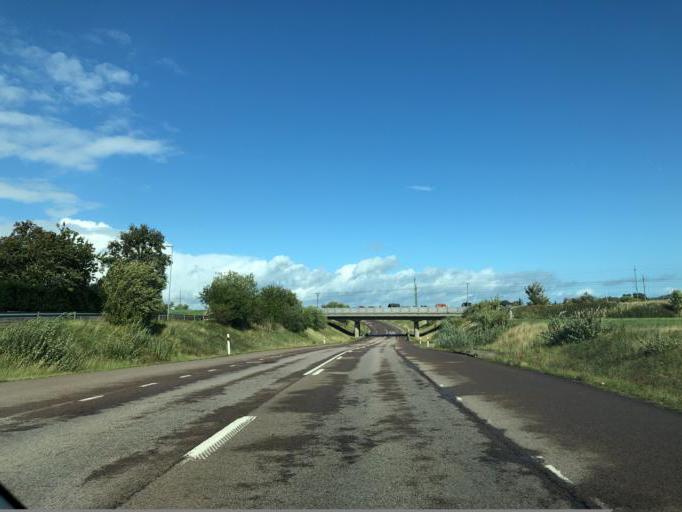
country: SE
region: Skane
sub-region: Helsingborg
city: Glumslov
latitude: 55.9175
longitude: 12.8312
